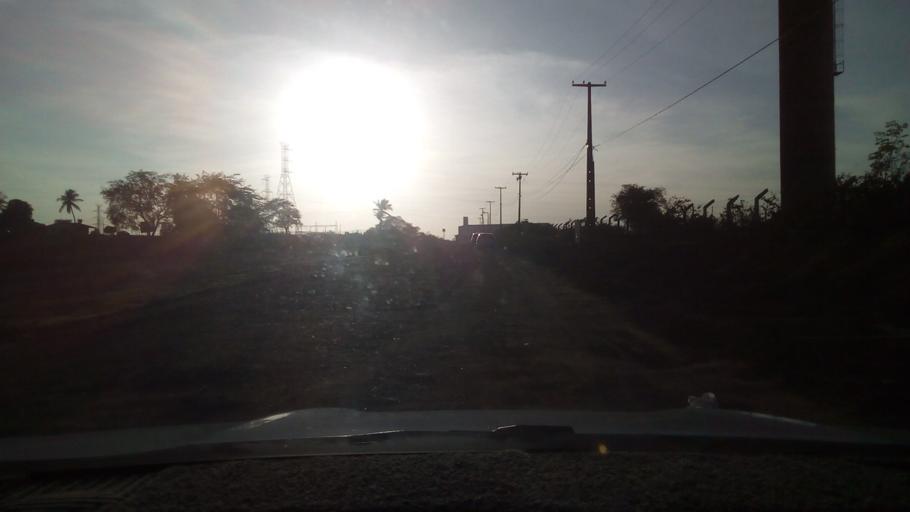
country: BR
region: Paraiba
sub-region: Conde
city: Conde
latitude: -7.1948
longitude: -34.8952
